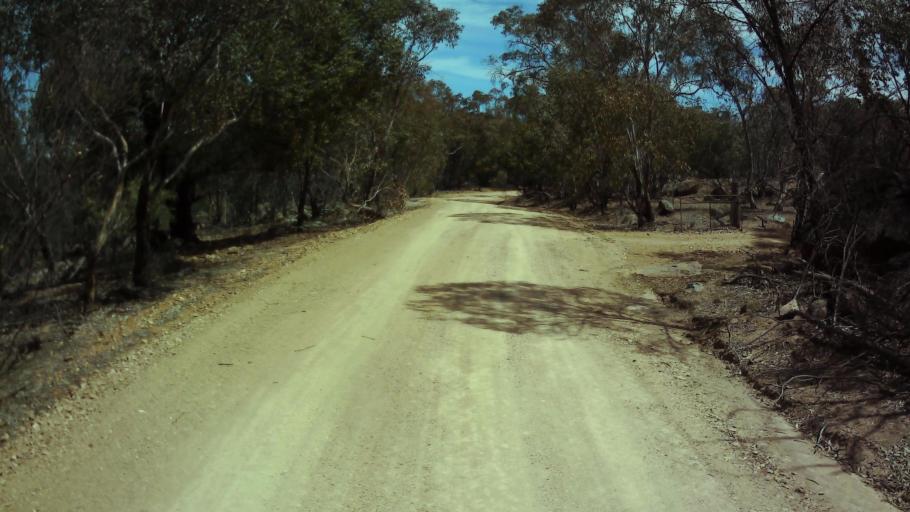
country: AU
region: New South Wales
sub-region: Weddin
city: Grenfell
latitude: -33.8068
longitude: 148.1601
